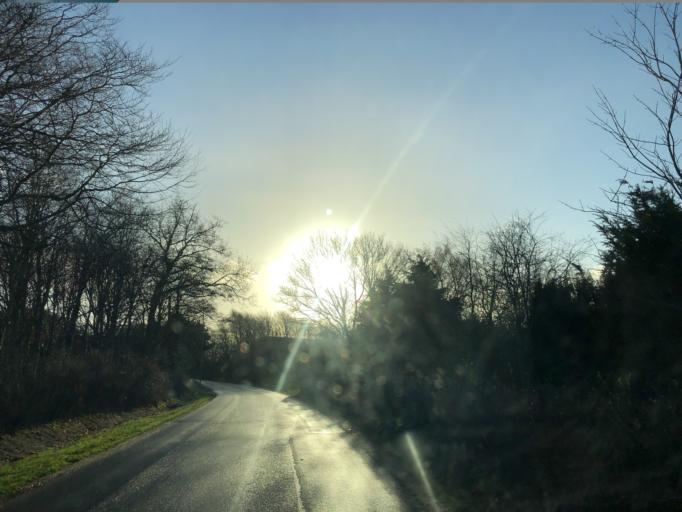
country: DK
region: Central Jutland
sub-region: Holstebro Kommune
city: Ulfborg
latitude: 56.2062
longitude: 8.2566
